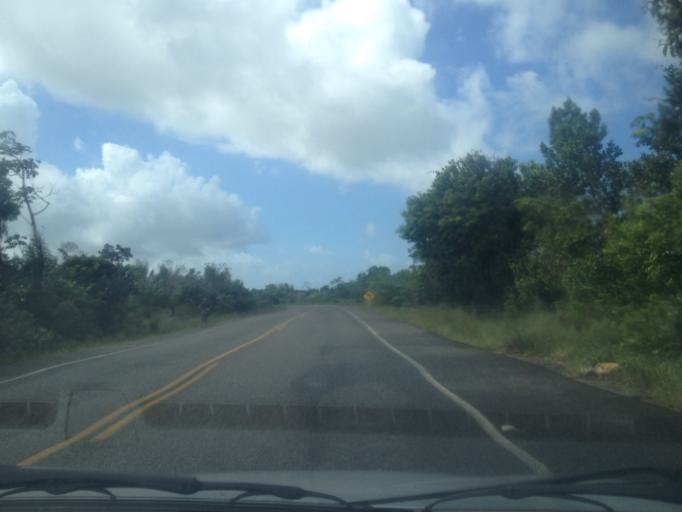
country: BR
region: Bahia
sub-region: Conde
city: Conde
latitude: -12.0832
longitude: -37.7673
